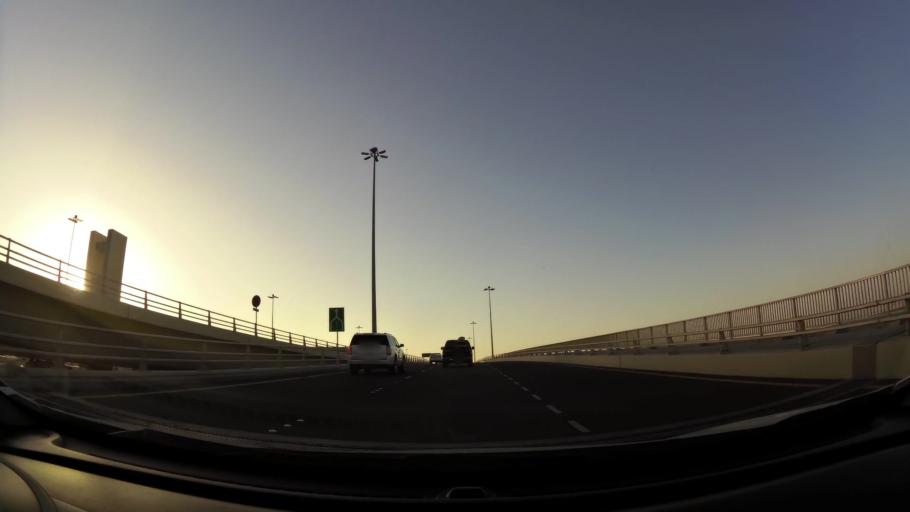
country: BH
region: Muharraq
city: Al Muharraq
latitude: 26.2478
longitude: 50.5889
